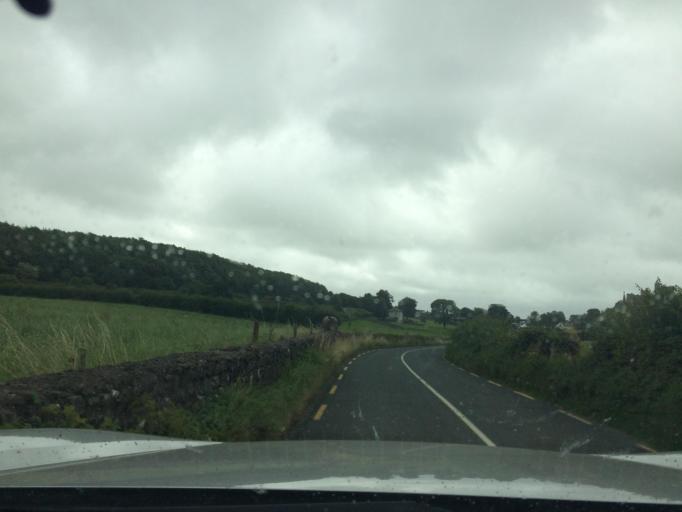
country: IE
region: Munster
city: Cashel
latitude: 52.5263
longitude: -7.8889
